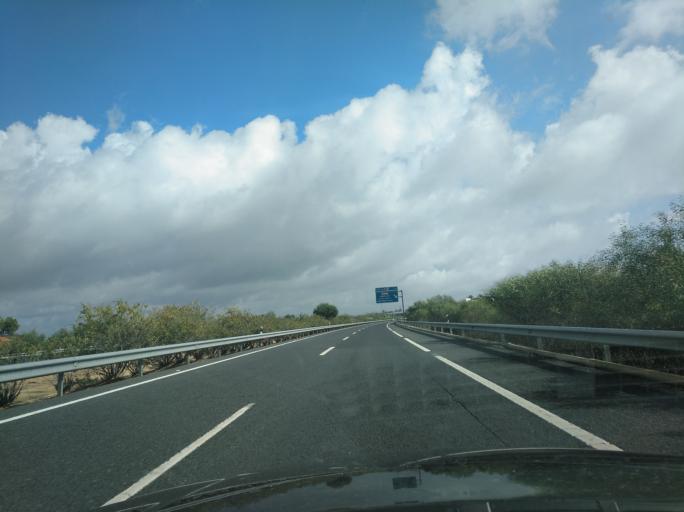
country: ES
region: Andalusia
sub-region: Provincia de Huelva
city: Lepe
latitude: 37.2925
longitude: -7.2288
